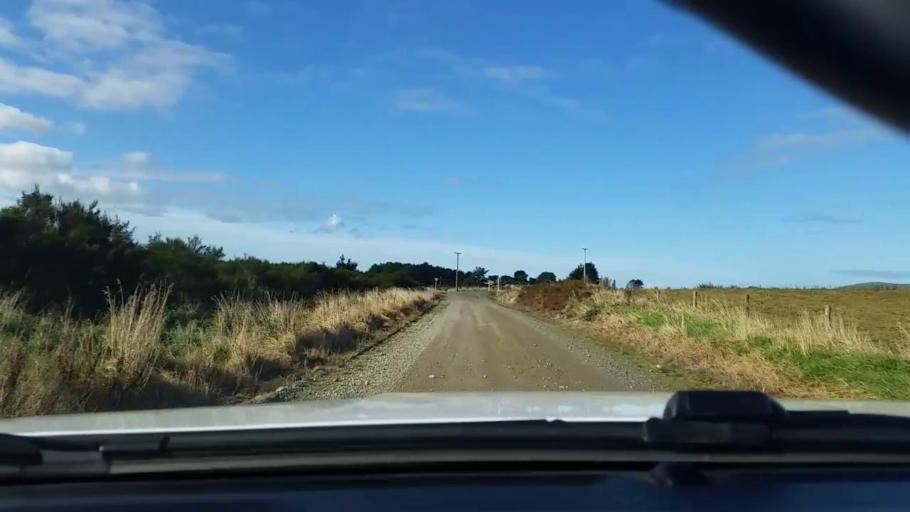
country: NZ
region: Southland
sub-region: Southland District
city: Riverton
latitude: -46.3329
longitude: 167.8199
